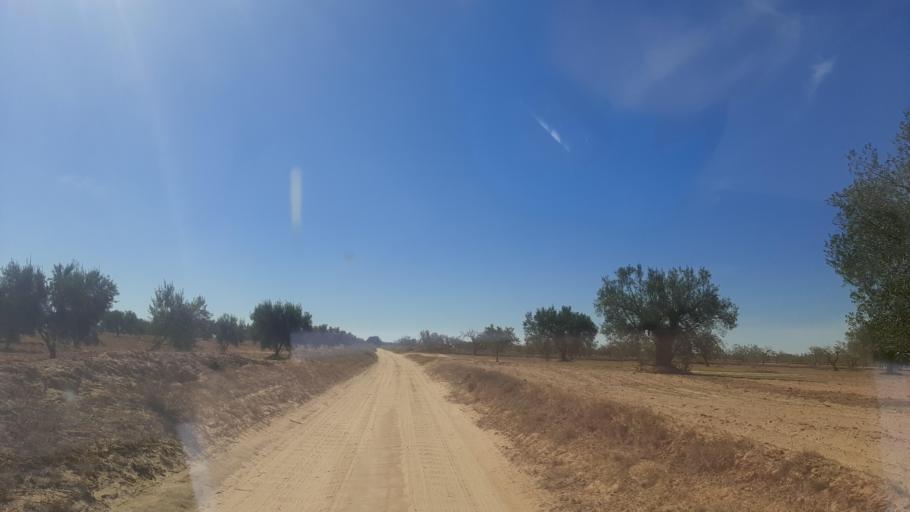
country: TN
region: Safaqis
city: Sfax
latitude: 34.8238
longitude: 10.5532
